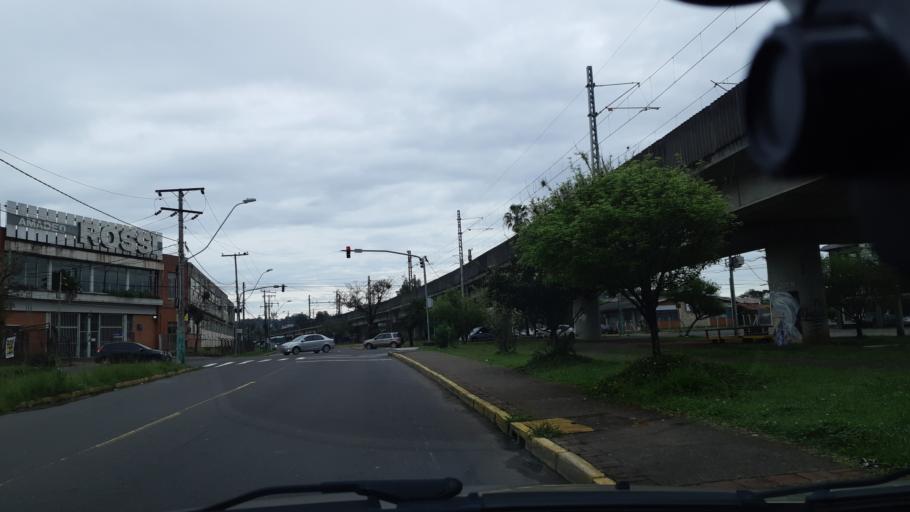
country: BR
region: Rio Grande do Sul
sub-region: Sao Leopoldo
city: Sao Leopoldo
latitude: -29.7725
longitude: -51.1430
